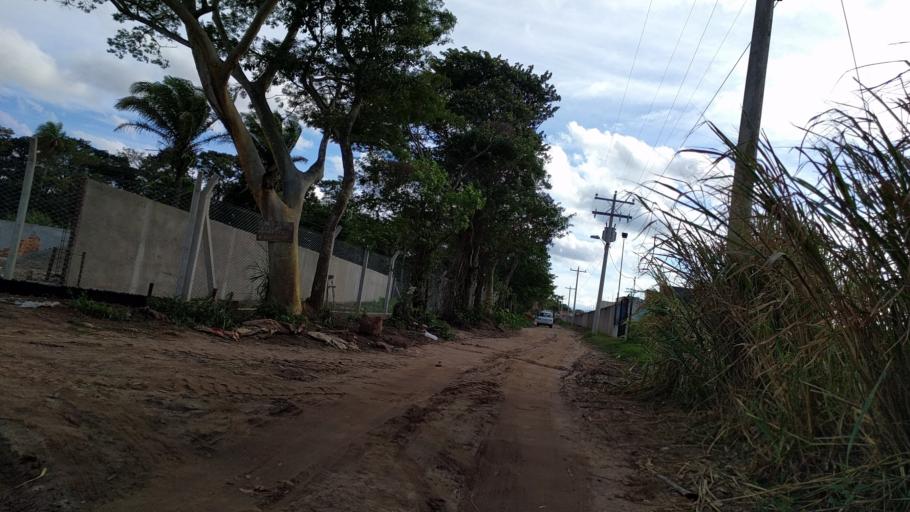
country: BO
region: Santa Cruz
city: Santa Cruz de la Sierra
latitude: -17.8506
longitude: -63.2563
